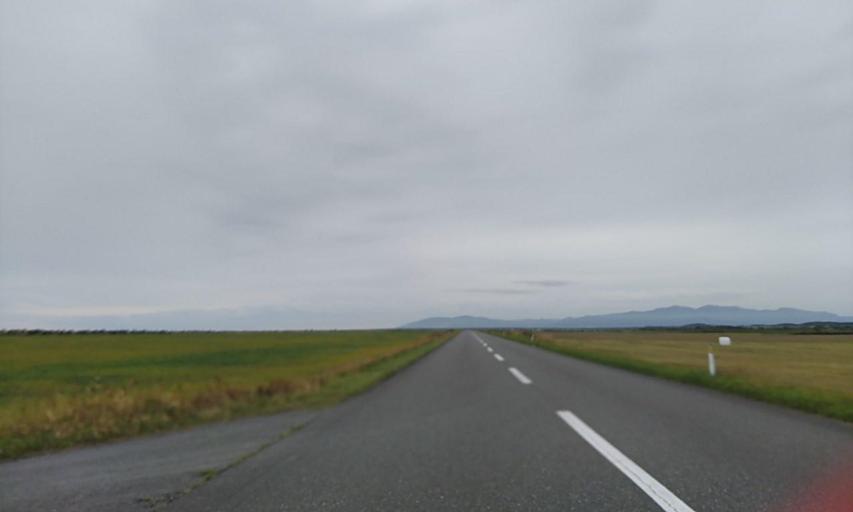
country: JP
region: Hokkaido
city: Makubetsu
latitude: 45.2000
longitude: 142.3008
